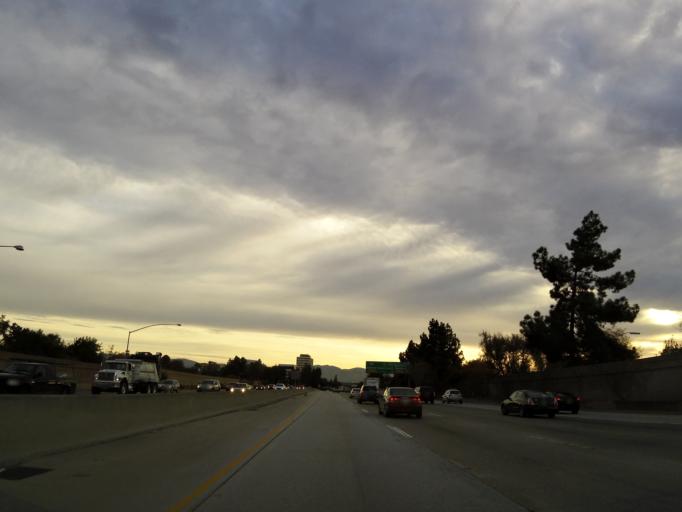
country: US
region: California
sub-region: Santa Clara County
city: Burbank
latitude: 37.3164
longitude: -121.9565
